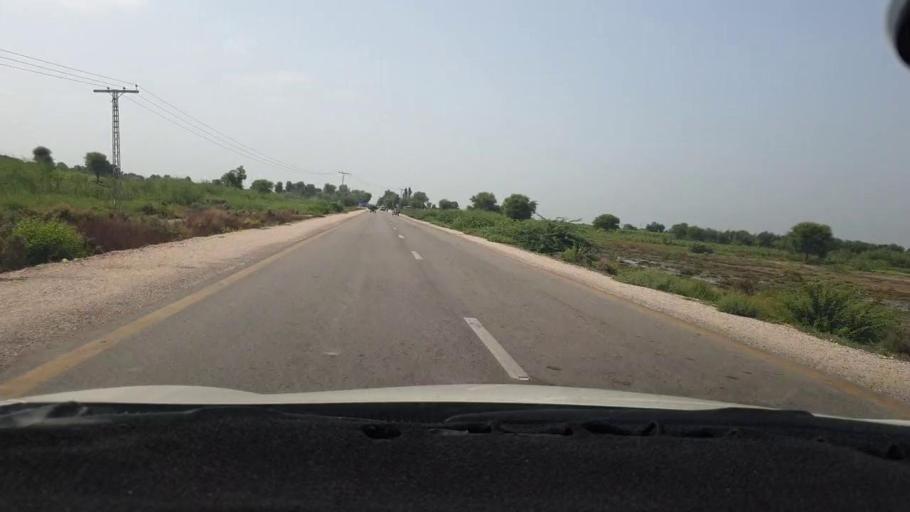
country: PK
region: Sindh
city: Mirpur Khas
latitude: 25.6448
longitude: 69.0963
